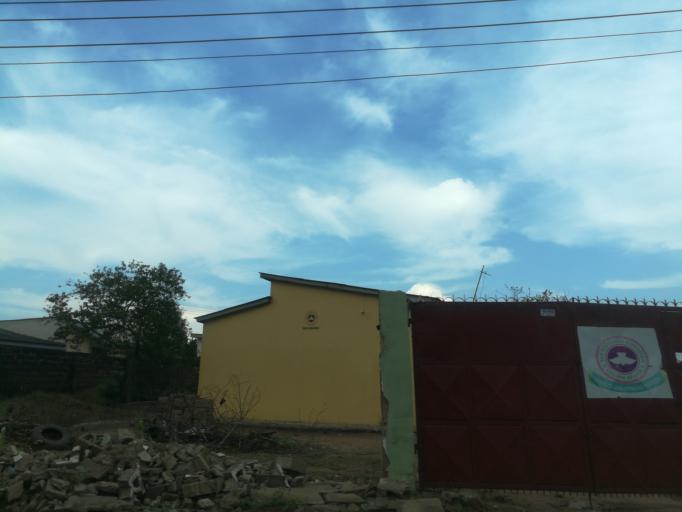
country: NG
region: Oyo
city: Ibadan
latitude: 7.4160
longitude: 3.9005
